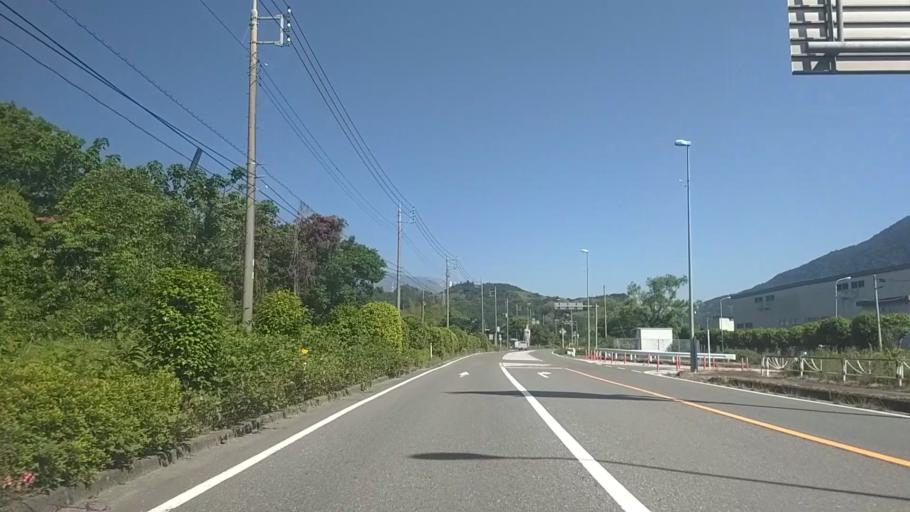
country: JP
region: Shizuoka
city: Fujinomiya
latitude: 35.2431
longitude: 138.4839
